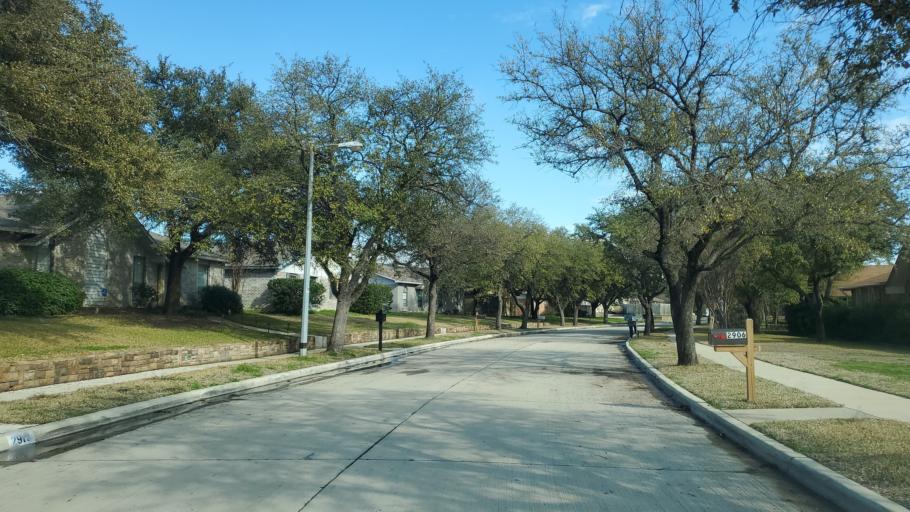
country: US
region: Texas
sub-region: Dallas County
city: Carrollton
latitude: 32.9953
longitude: -96.8779
